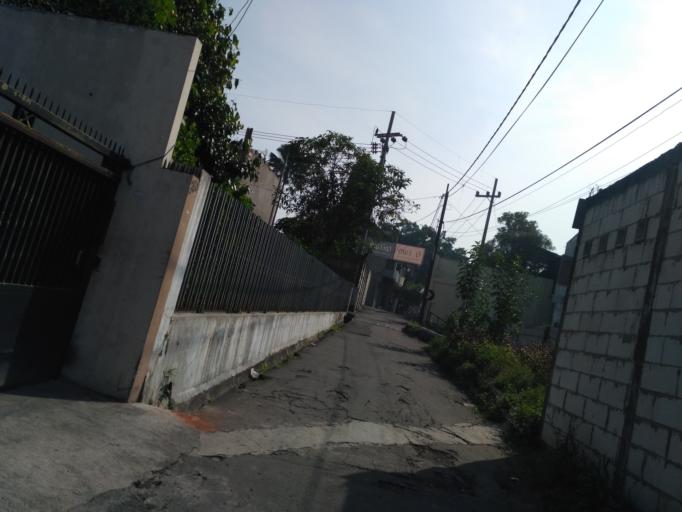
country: ID
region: East Java
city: Malang
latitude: -7.9784
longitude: 112.6197
